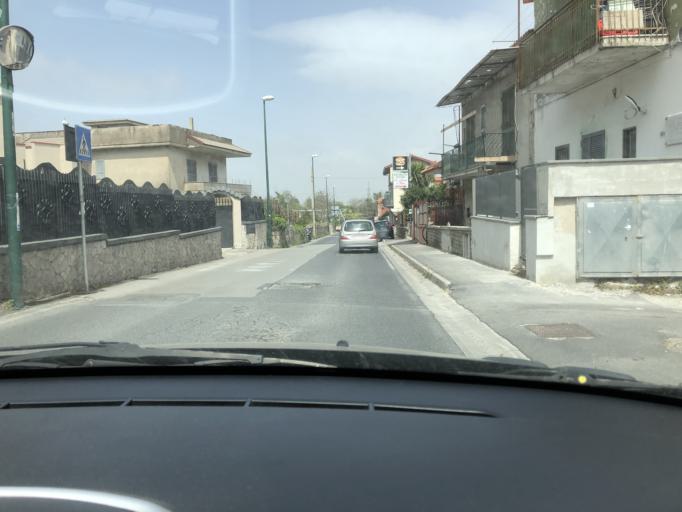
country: IT
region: Campania
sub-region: Provincia di Napoli
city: Torre Caracciolo
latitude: 40.8741
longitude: 14.1869
